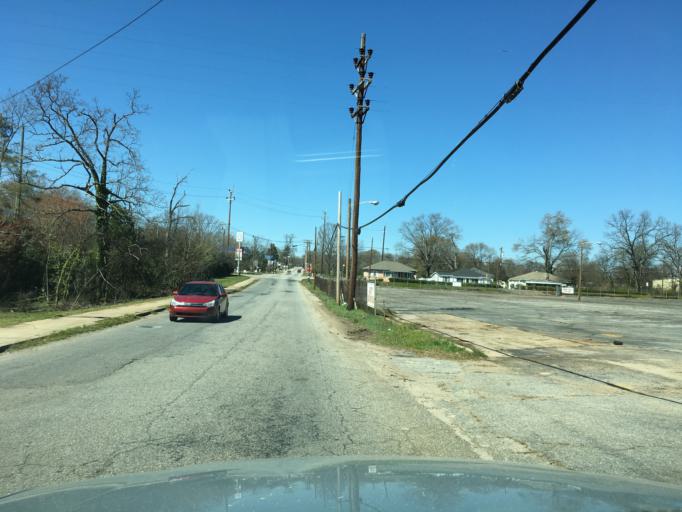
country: US
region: South Carolina
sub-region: Spartanburg County
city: Saxon
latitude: 34.9626
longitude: -81.9679
